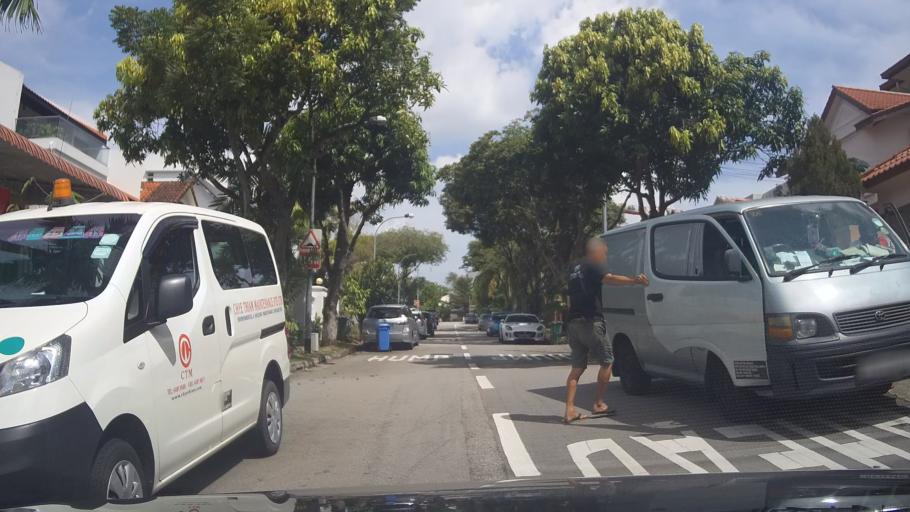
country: MY
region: Johor
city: Kampung Pasir Gudang Baru
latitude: 1.3964
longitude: 103.8738
